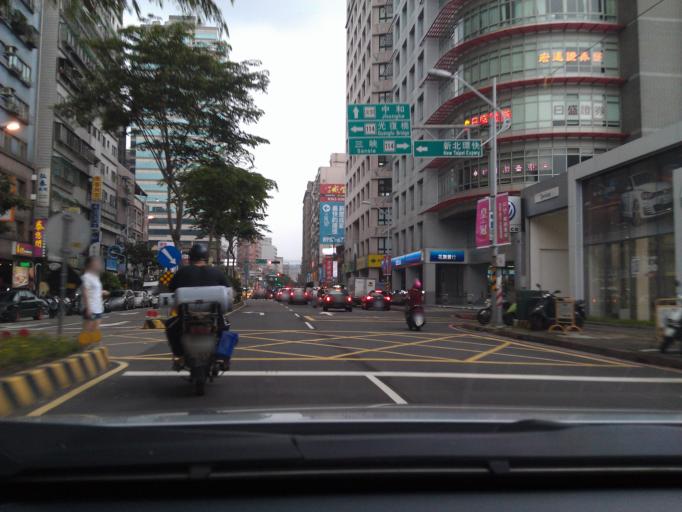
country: TW
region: Taipei
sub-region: Taipei
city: Banqiao
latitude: 25.0200
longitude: 121.4792
